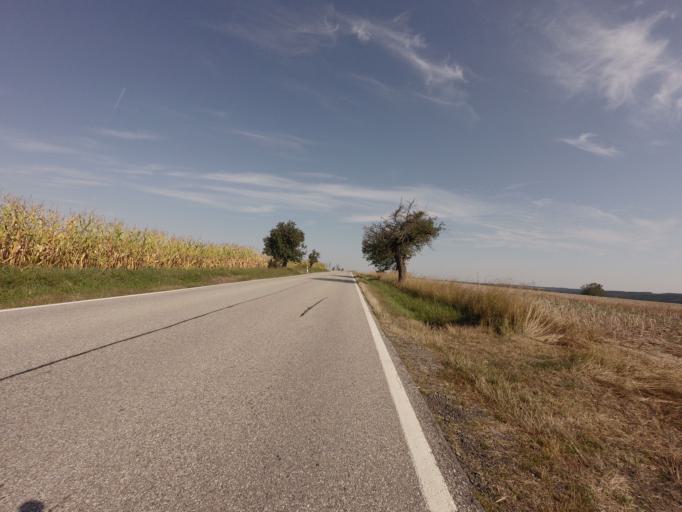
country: CZ
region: Jihocesky
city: Bernartice
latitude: 49.2996
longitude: 14.3847
